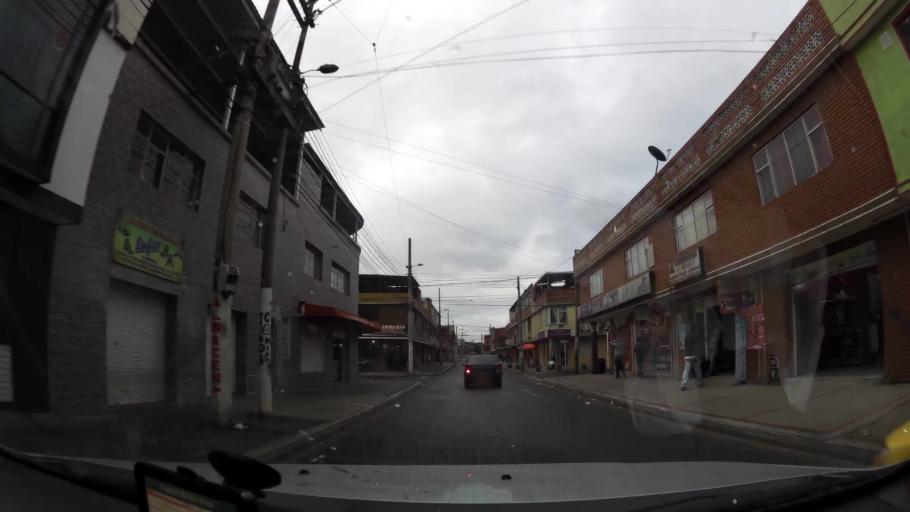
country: CO
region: Bogota D.C.
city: Bogota
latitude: 4.5927
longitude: -74.1358
